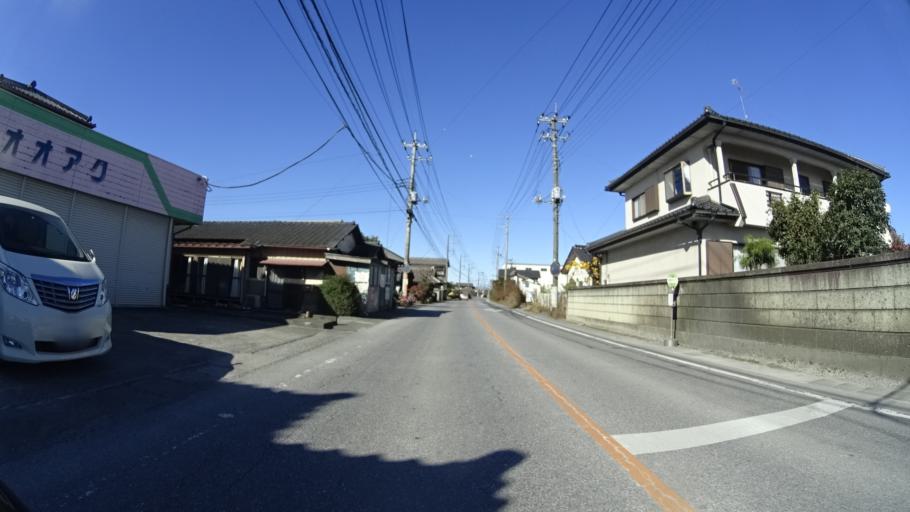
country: JP
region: Tochigi
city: Mibu
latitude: 36.4558
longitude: 139.7542
